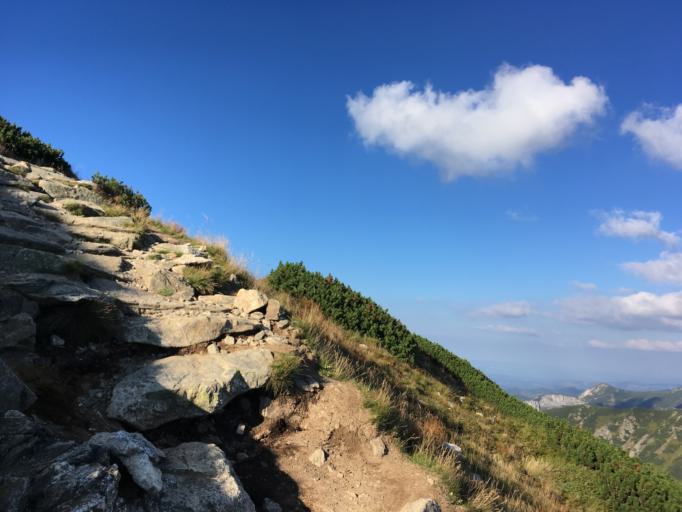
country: PL
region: Lesser Poland Voivodeship
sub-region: Powiat tatrzanski
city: Zakopane
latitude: 49.2342
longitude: 19.9432
